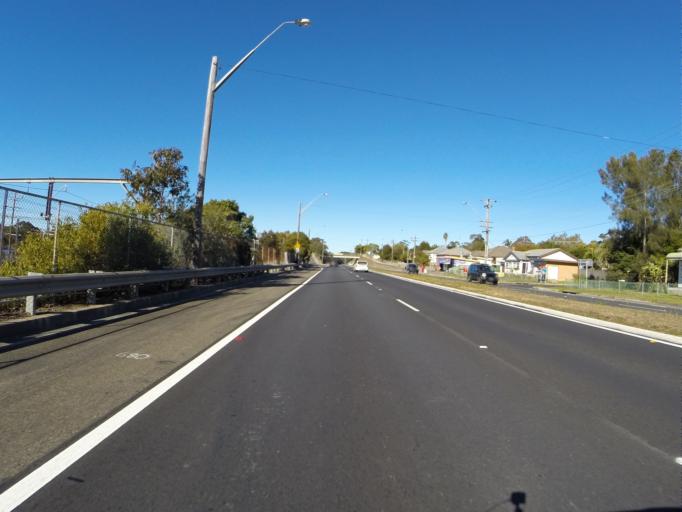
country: AU
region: New South Wales
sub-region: Wollongong
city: Helensburgh
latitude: -34.1331
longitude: 150.9939
